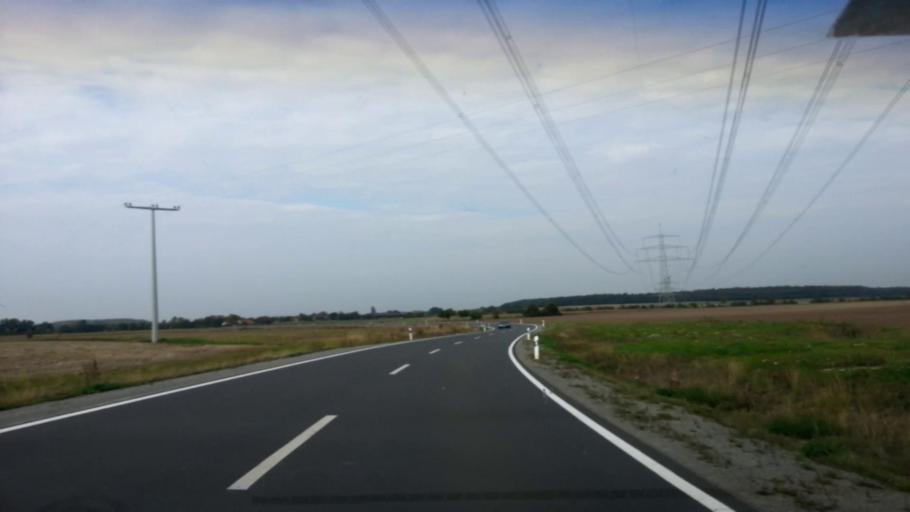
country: DE
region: Bavaria
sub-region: Regierungsbezirk Unterfranken
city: Castell
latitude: 49.7588
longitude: 10.3369
